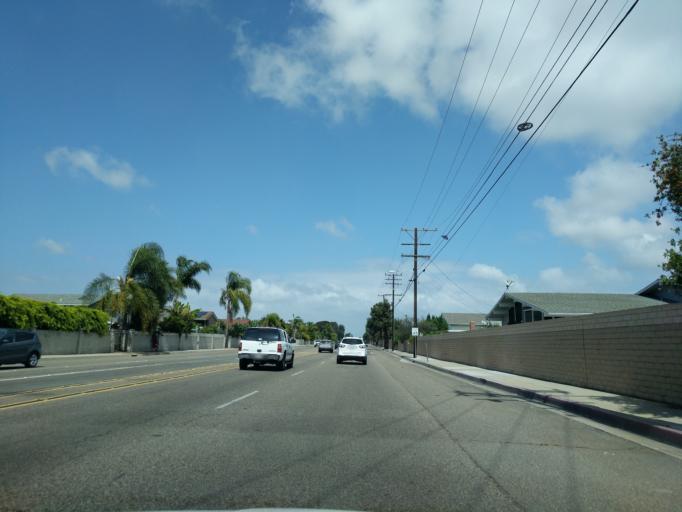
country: US
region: California
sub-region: Orange County
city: Midway City
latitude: 33.7085
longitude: -118.0238
